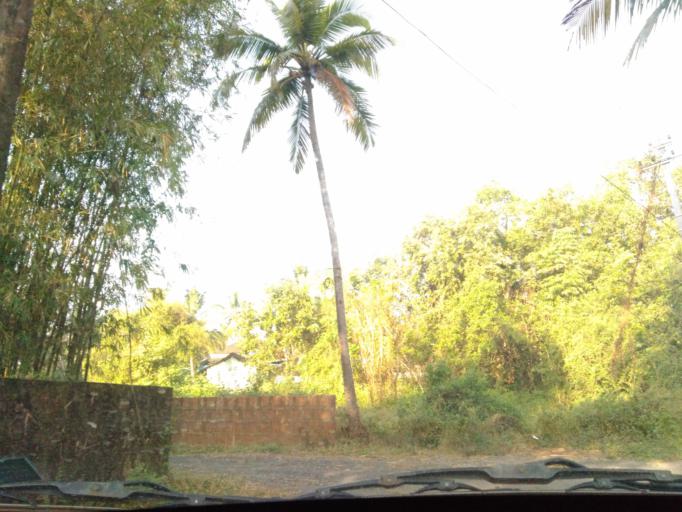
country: IN
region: Goa
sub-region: South Goa
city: Chinchinim
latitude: 15.2098
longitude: 73.9741
